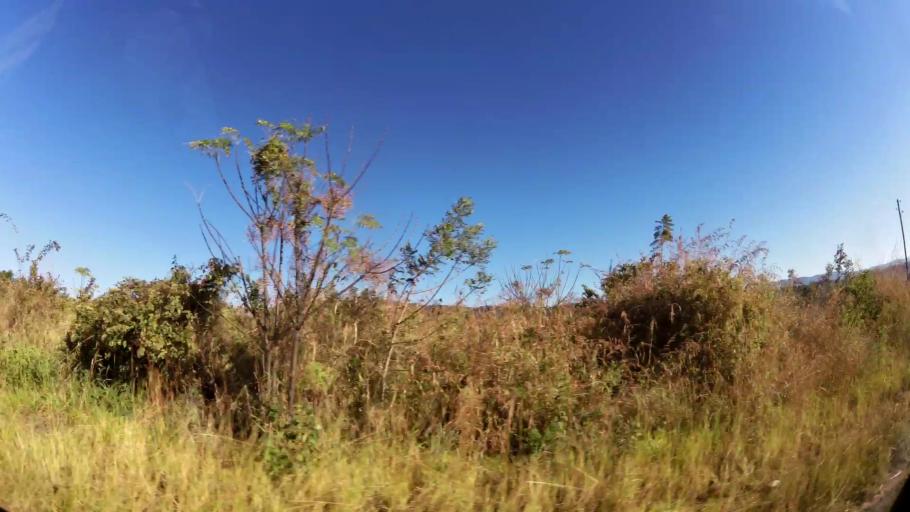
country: ZA
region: Limpopo
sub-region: Mopani District Municipality
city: Tzaneen
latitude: -23.8594
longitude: 30.1098
